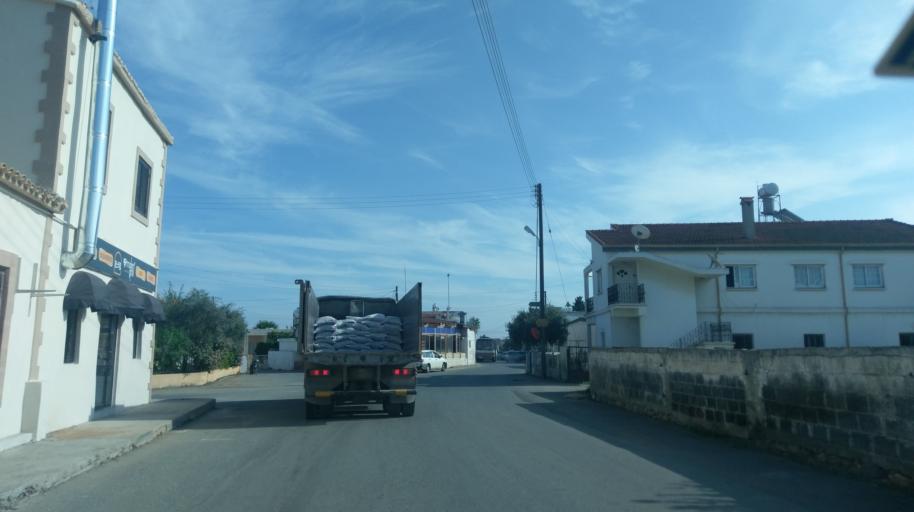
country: CY
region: Ammochostos
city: Trikomo
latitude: 35.1959
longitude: 33.8743
